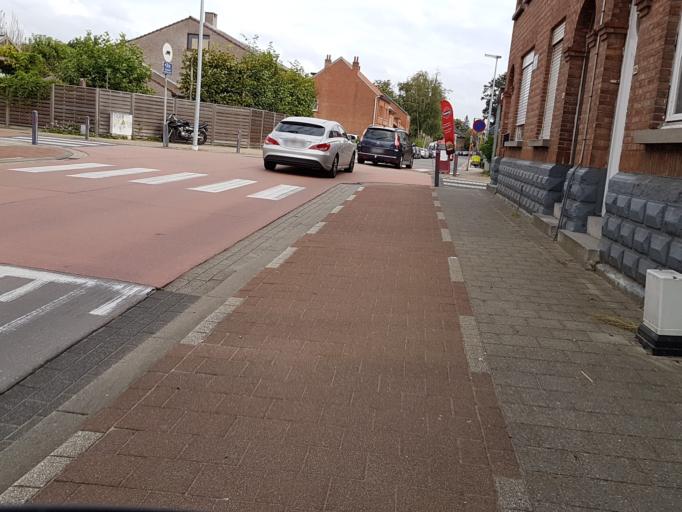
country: BE
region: Flanders
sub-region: Provincie Vlaams-Brabant
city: Haacht
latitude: 50.9602
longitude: 4.6285
